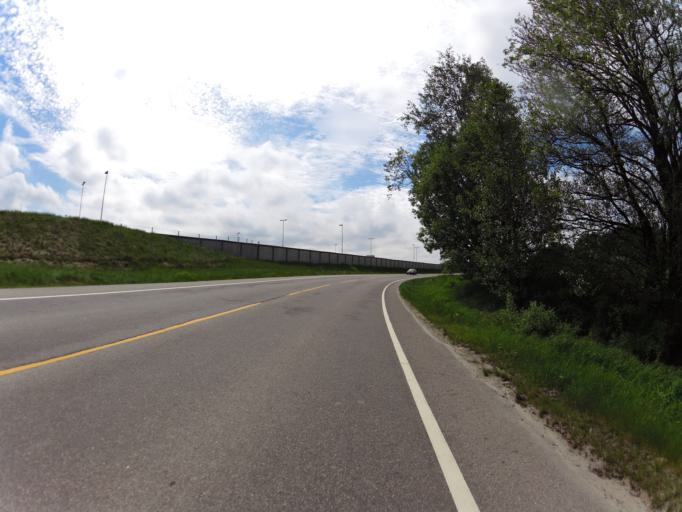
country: NO
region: Ostfold
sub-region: Rade
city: Karlshus
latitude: 59.3256
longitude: 10.9535
